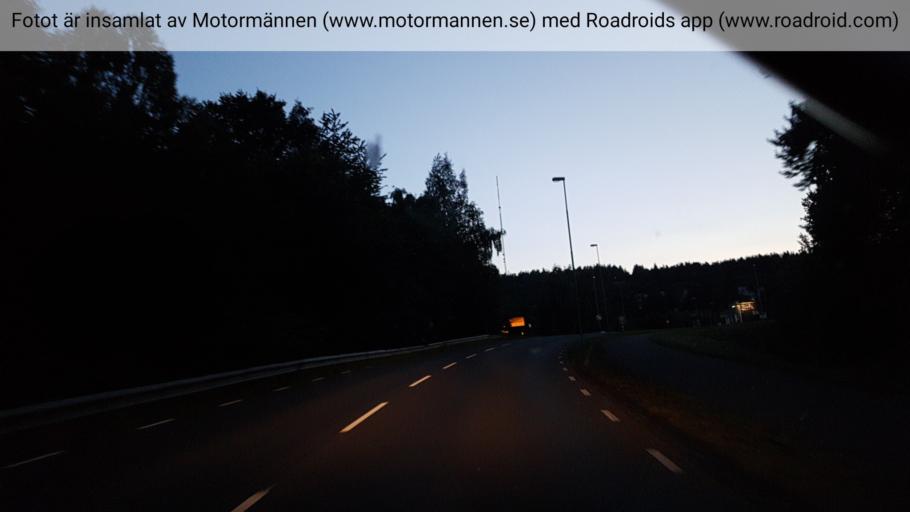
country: SE
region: Vaestra Goetaland
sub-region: Skovde Kommun
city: Skoevde
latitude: 58.4101
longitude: 13.8387
